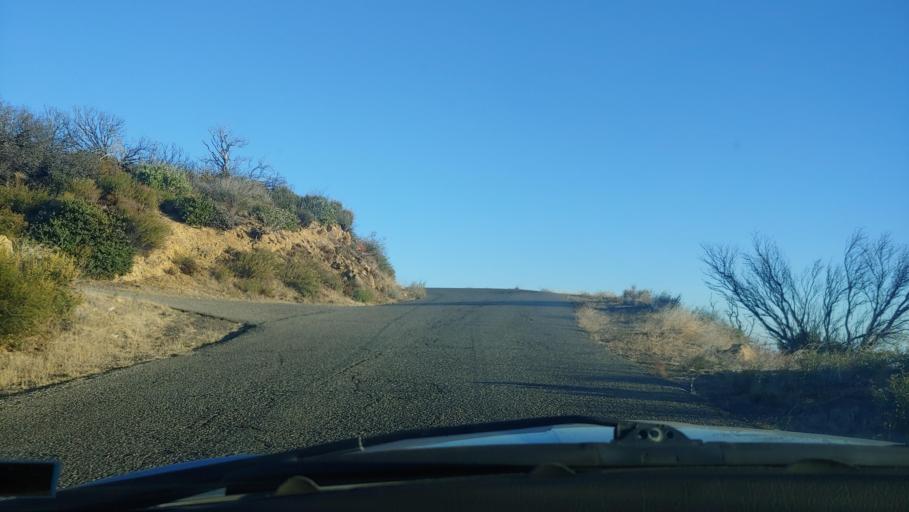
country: US
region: California
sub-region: Santa Barbara County
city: Mission Canyon
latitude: 34.5089
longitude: -119.7723
